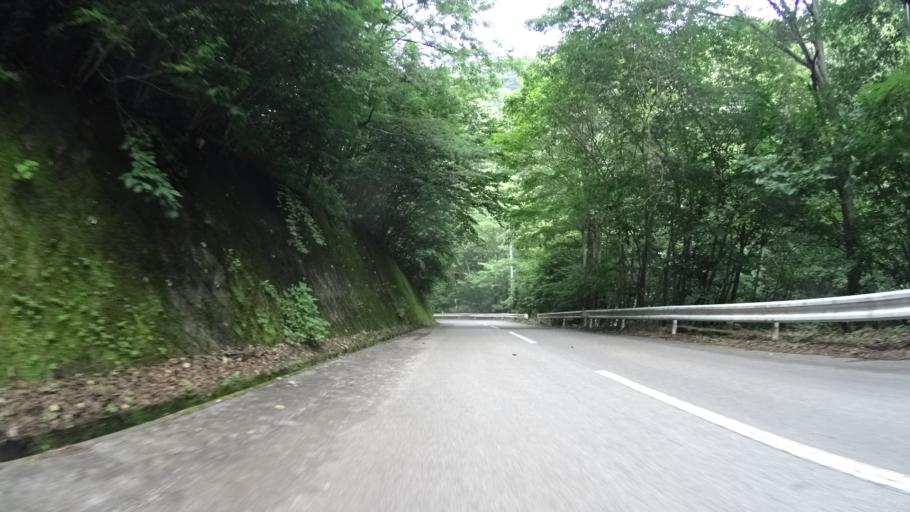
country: JP
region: Nagano
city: Saku
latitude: 36.1180
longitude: 138.6140
